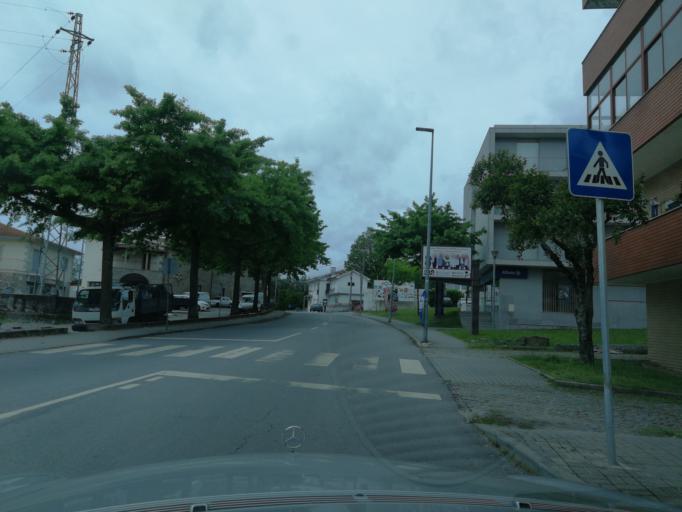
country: PT
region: Braga
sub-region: Amares
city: Amares
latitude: 41.6259
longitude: -8.3628
